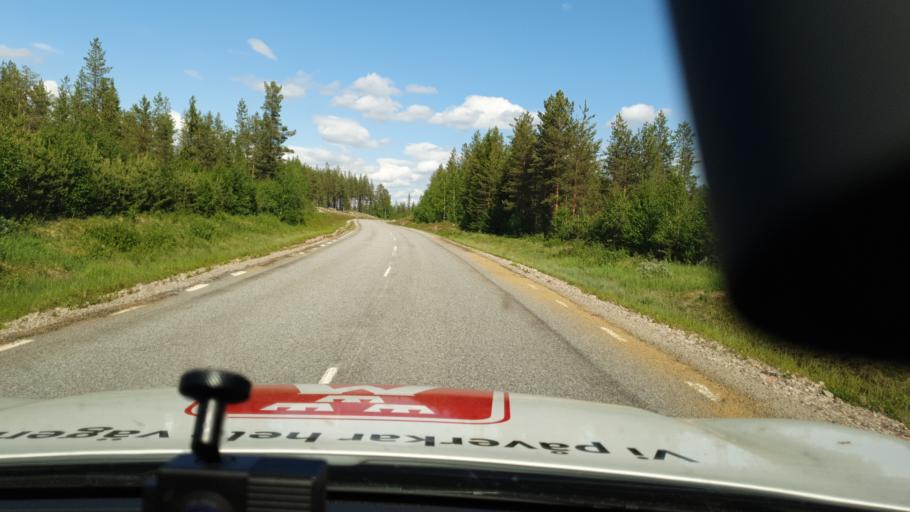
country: SE
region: Vaesterbotten
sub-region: Lycksele Kommun
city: Soderfors
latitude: 64.9346
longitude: 18.2886
